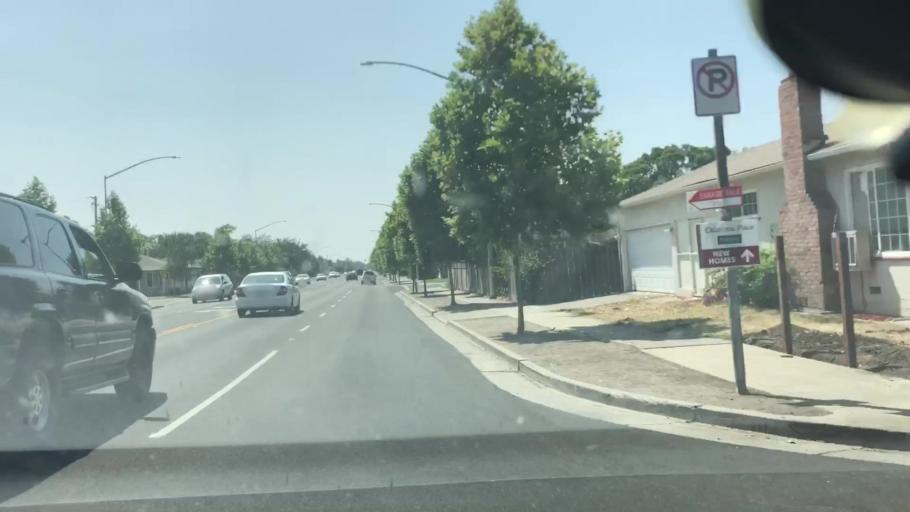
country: US
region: California
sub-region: San Joaquin County
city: Lincoln Village
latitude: 37.9898
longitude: -121.3034
